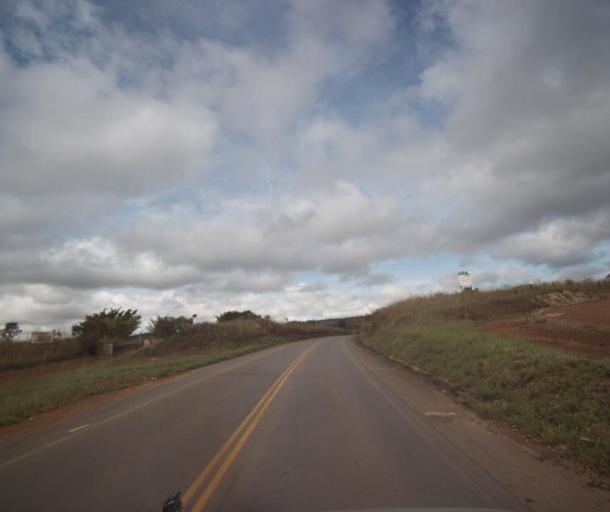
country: BR
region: Goias
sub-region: Pirenopolis
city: Pirenopolis
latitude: -15.8271
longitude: -48.7787
